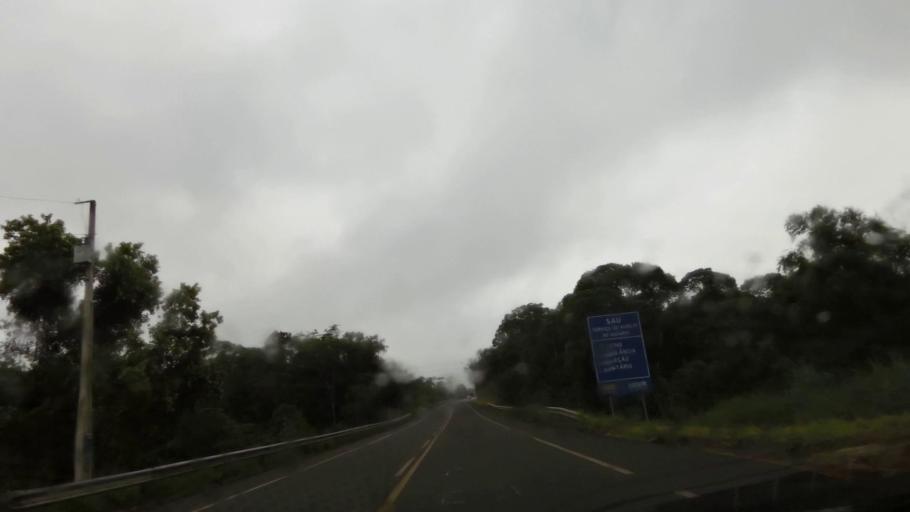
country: BR
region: Espirito Santo
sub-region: Guarapari
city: Guarapari
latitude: -20.6367
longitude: -40.5281
